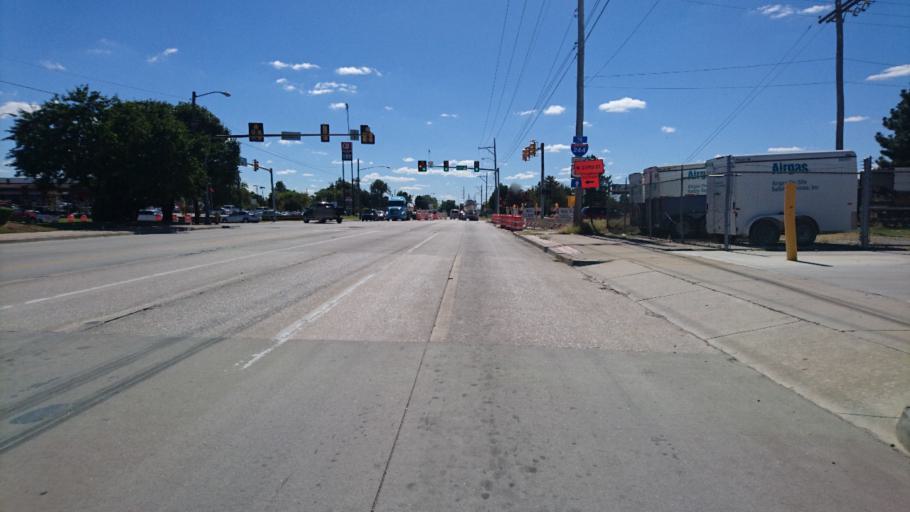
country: US
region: Oklahoma
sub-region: Tulsa County
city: Tulsa
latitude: 36.1304
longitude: -96.0071
